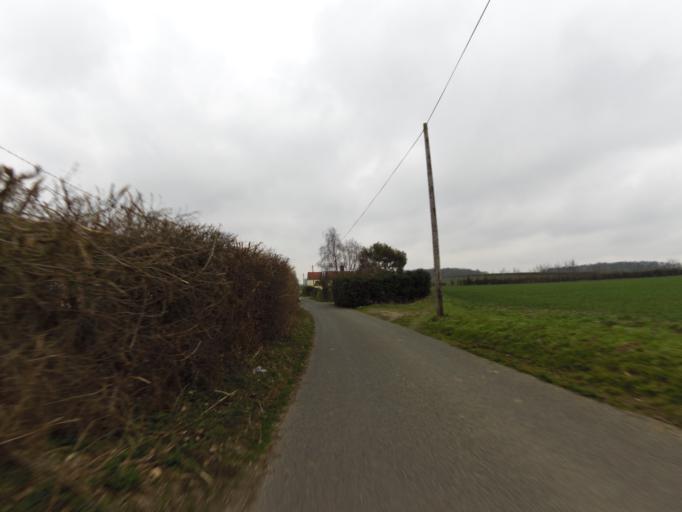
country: GB
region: England
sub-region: Suffolk
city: Framlingham
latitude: 52.2083
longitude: 1.3302
